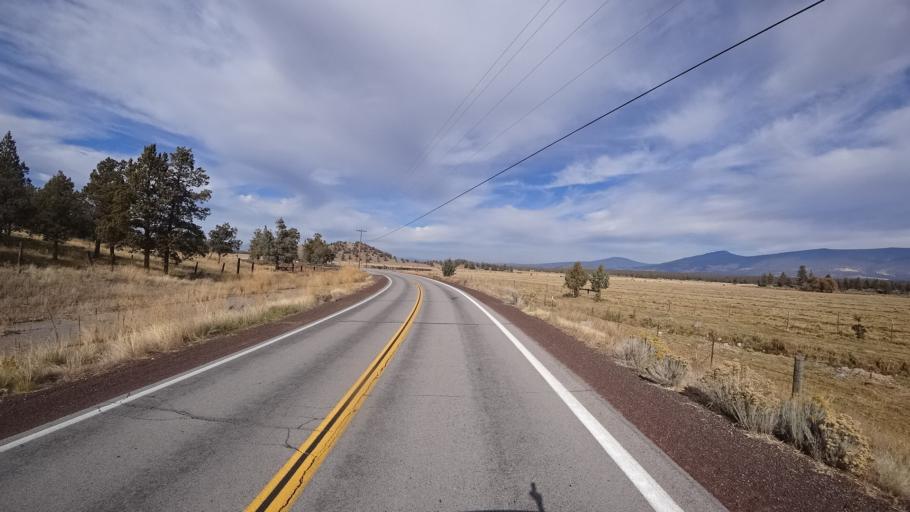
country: US
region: California
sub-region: Siskiyou County
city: Weed
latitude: 41.5652
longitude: -122.3864
